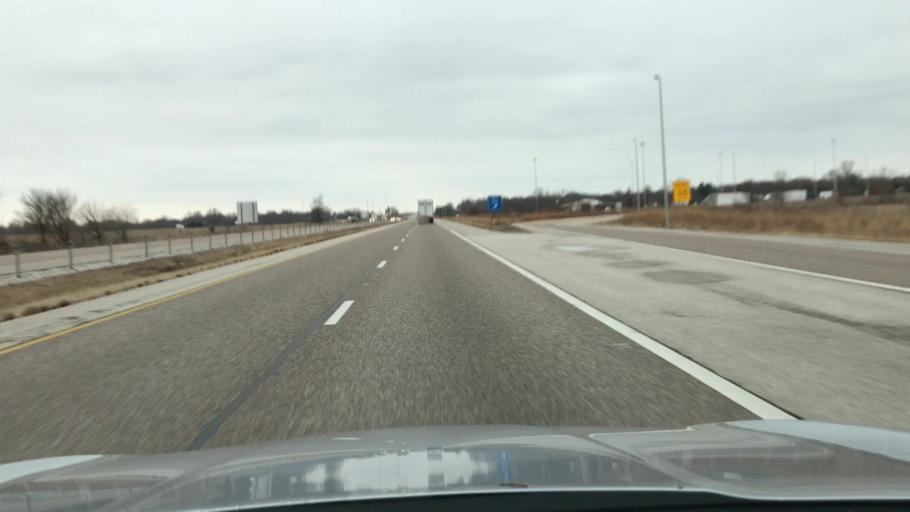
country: US
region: Illinois
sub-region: Madison County
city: Worden
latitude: 38.8753
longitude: -89.8479
